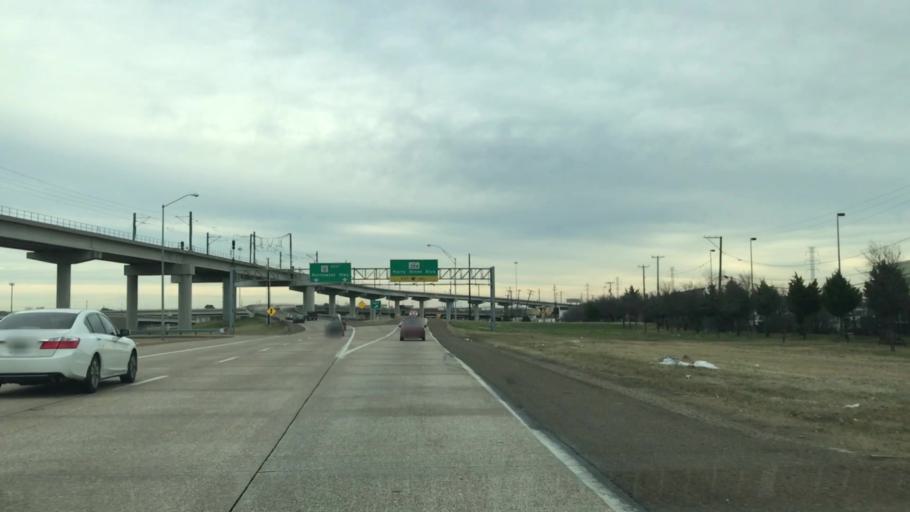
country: US
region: Texas
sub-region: Dallas County
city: Farmers Branch
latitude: 32.8548
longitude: -96.8846
